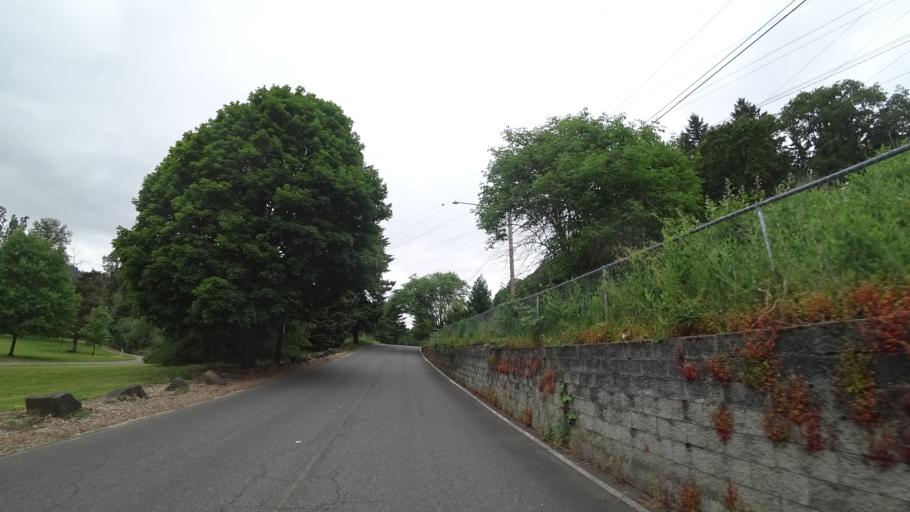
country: US
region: Oregon
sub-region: Clackamas County
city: Milwaukie
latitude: 45.4663
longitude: -122.6624
